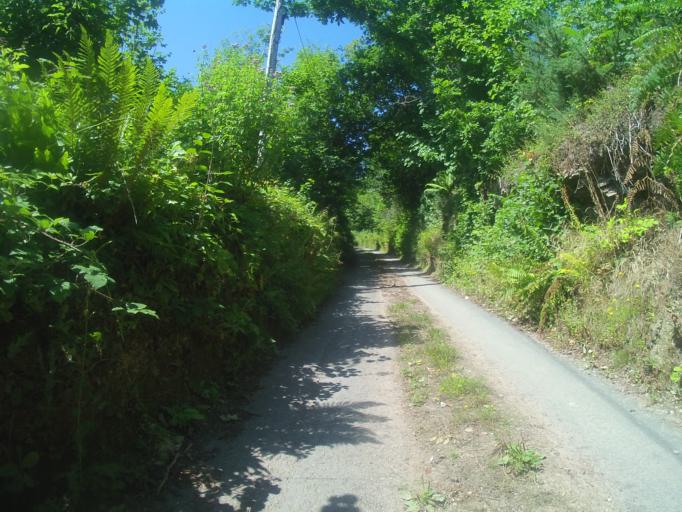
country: GB
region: England
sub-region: Devon
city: Dartmouth
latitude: 50.3583
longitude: -3.6152
